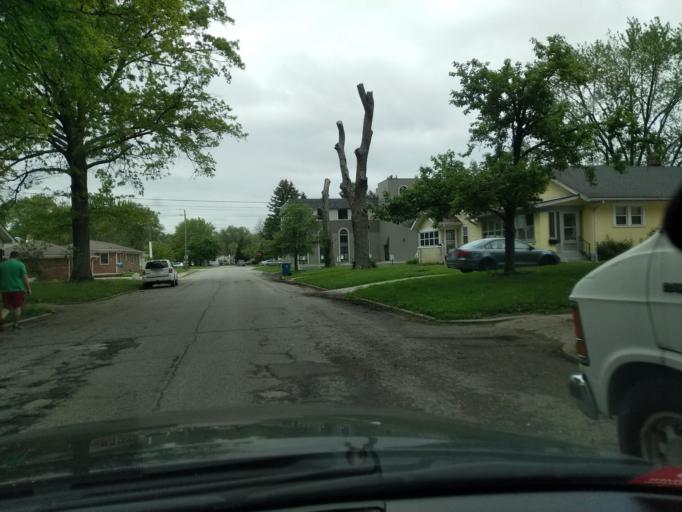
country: US
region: Indiana
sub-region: Marion County
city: Broad Ripple
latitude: 39.8467
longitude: -86.1278
